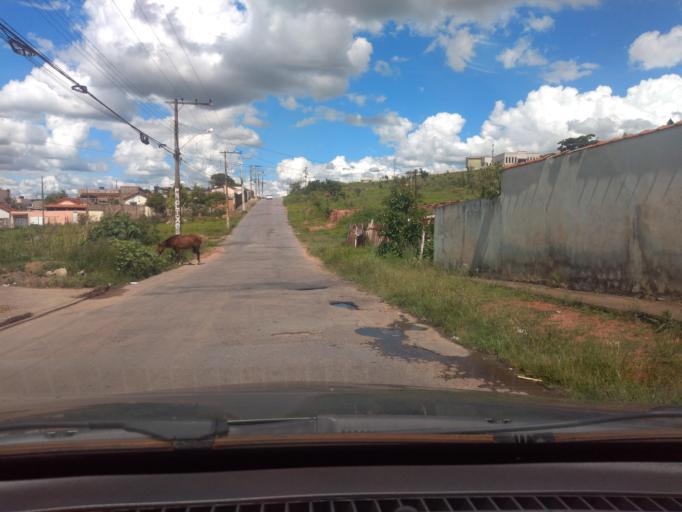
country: BR
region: Minas Gerais
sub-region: Tres Coracoes
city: Tres Coracoes
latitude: -21.6827
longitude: -45.2465
